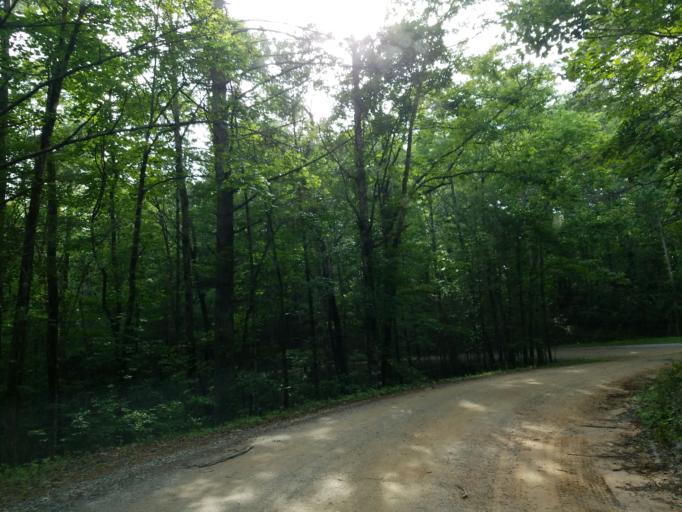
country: US
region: Georgia
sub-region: Union County
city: Blairsville
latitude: 34.7492
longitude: -84.0680
